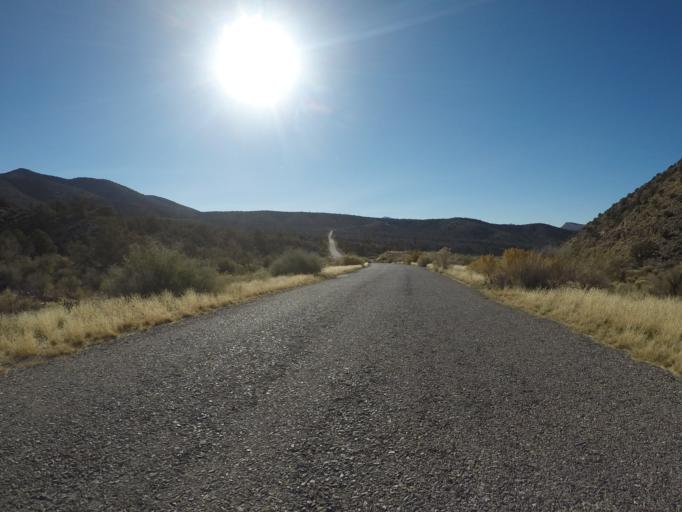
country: US
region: Nevada
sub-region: Clark County
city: Summerlin South
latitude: 36.0963
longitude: -115.5662
